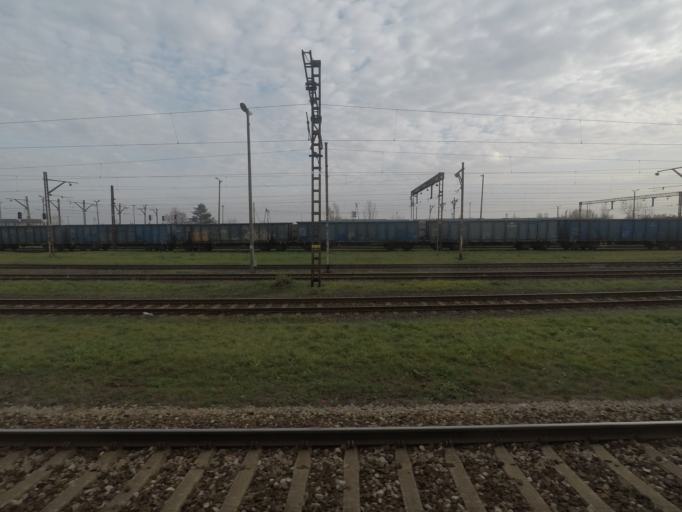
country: PL
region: Subcarpathian Voivodeship
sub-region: Powiat przemyski
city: Orly
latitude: 49.8399
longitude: 22.8430
